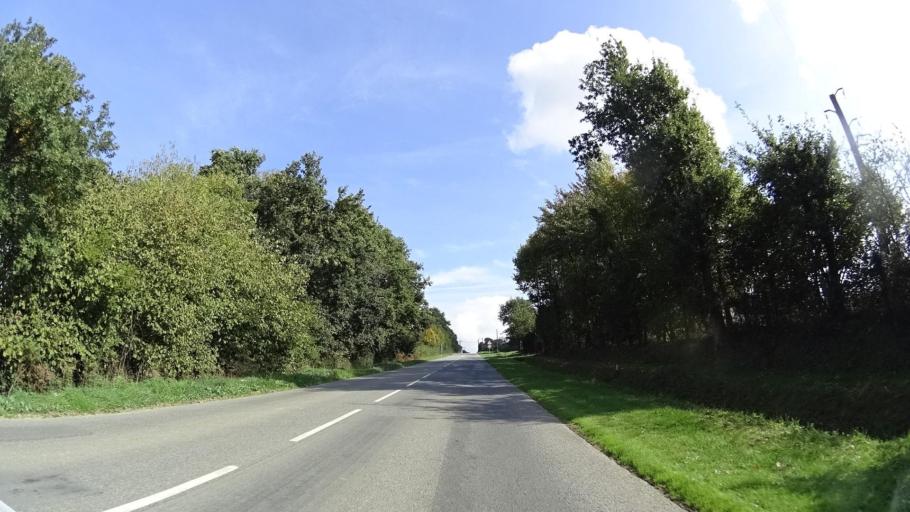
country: FR
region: Brittany
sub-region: Departement des Cotes-d'Armor
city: Plouasne
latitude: 48.2847
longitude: -1.9864
